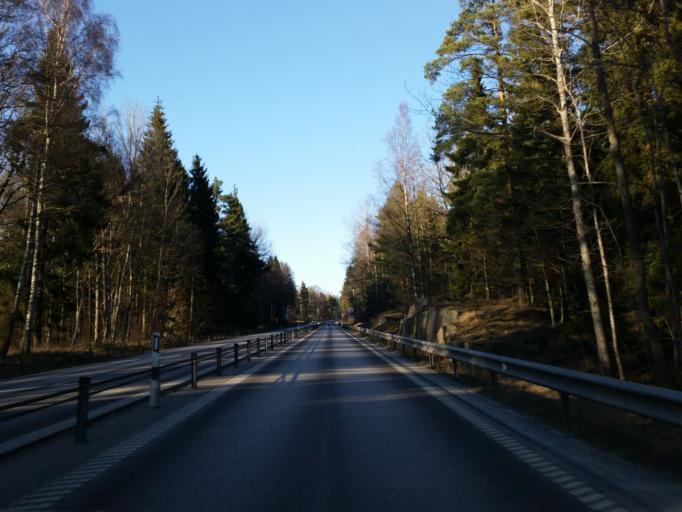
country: SE
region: Kalmar
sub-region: Oskarshamns Kommun
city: Oskarshamn
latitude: 57.3294
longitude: 16.4773
